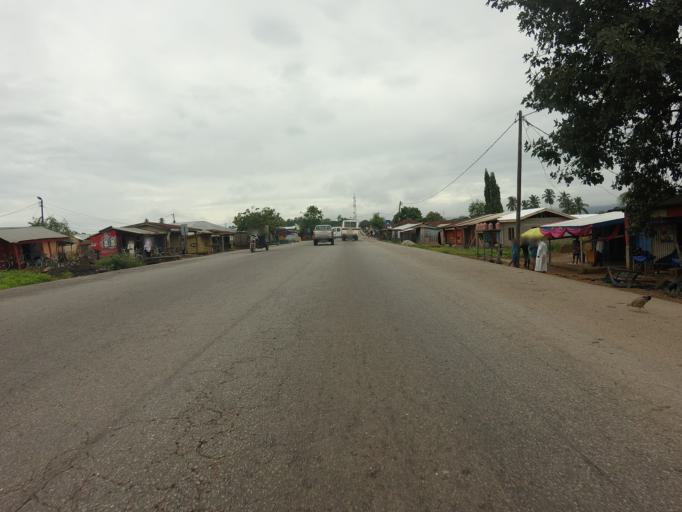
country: GH
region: Eastern
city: Begoro
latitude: 6.4319
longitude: -0.5836
